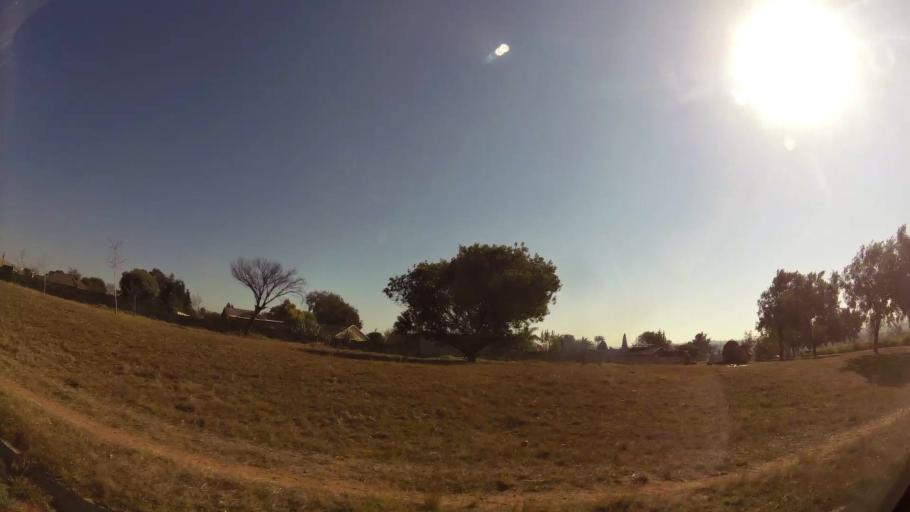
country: ZA
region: Gauteng
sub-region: Ekurhuleni Metropolitan Municipality
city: Germiston
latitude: -26.2449
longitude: 28.1101
